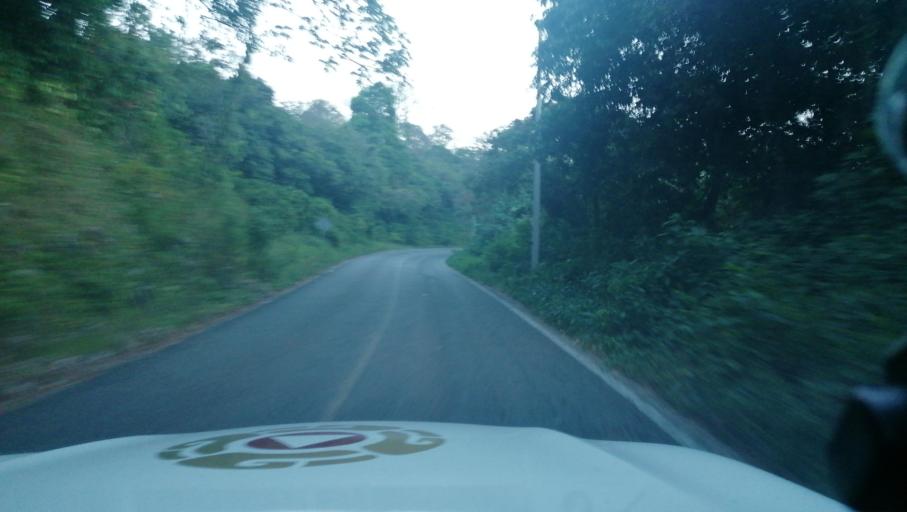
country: MX
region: Chiapas
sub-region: Cacahoatan
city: Benito Juarez
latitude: 15.0365
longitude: -92.2432
